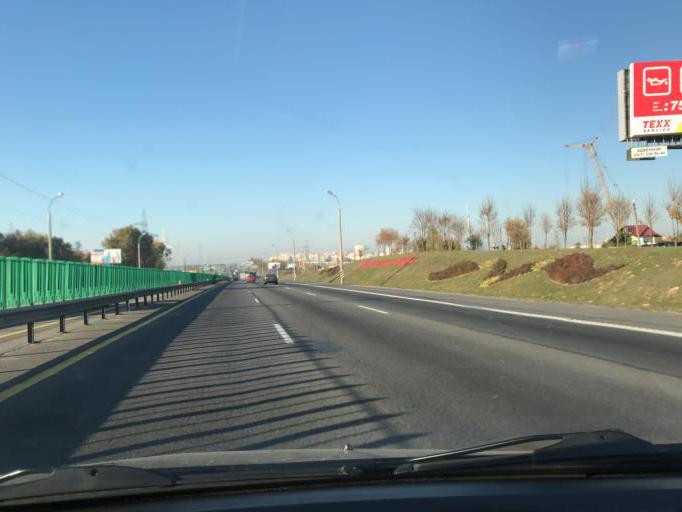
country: BY
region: Minsk
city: Malinovka
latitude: 53.8645
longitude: 27.4255
